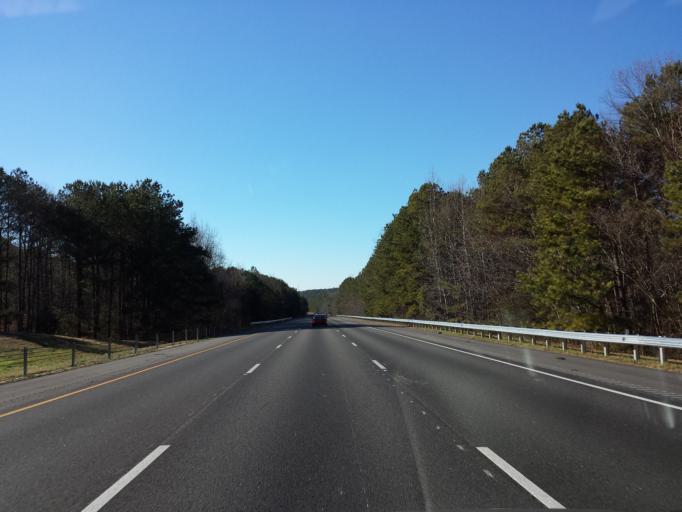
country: US
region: Georgia
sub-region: Douglas County
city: Douglasville
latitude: 33.7226
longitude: -84.7826
